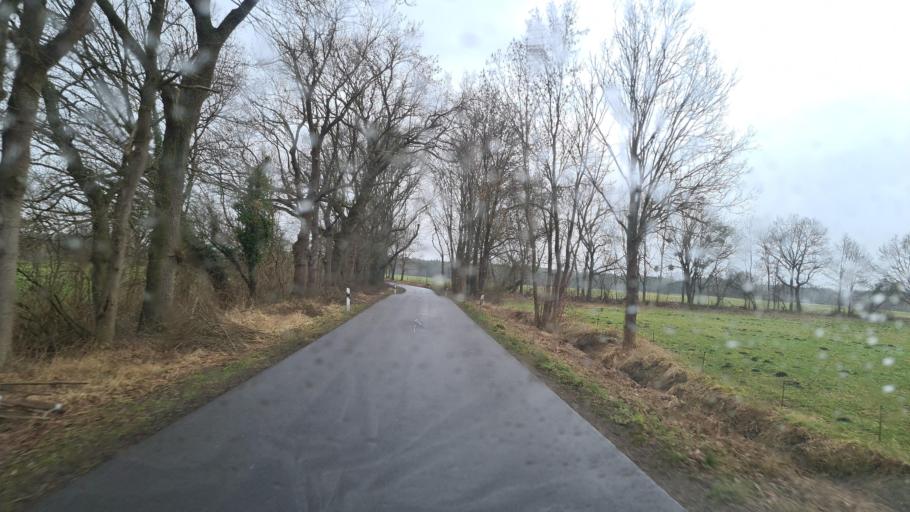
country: DE
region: Brandenburg
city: Oranienburg
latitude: 52.8774
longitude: 13.2189
